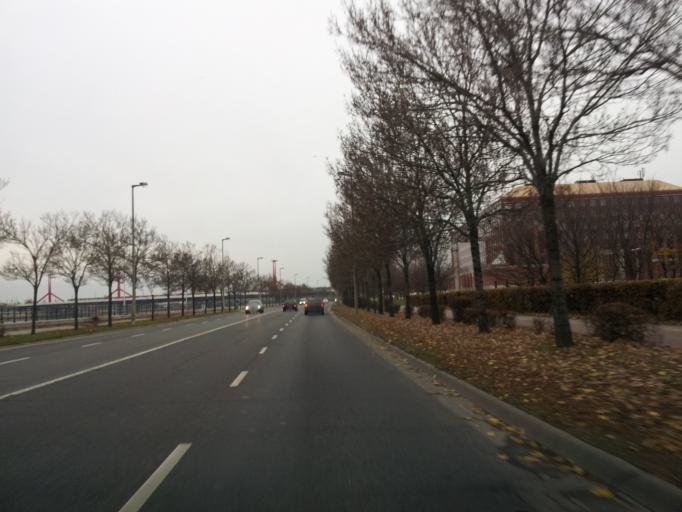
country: HU
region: Budapest
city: Budapest IX. keruelet
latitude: 47.4746
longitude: 19.0631
